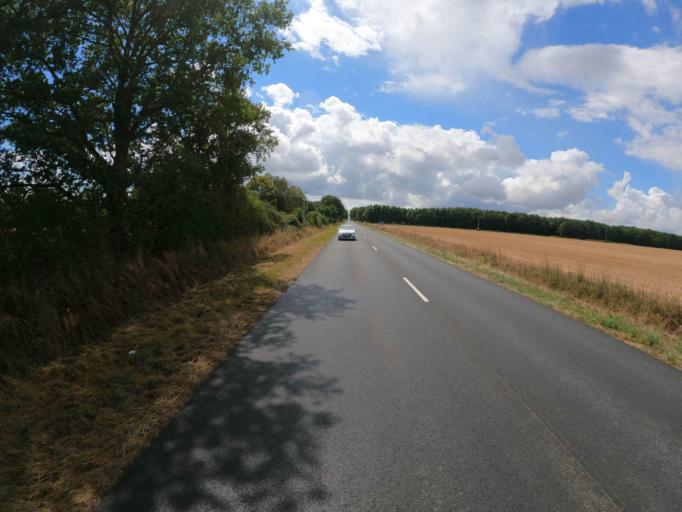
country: FR
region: Pays de la Loire
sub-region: Departement de Maine-et-Loire
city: Feneu
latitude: 47.5877
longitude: -0.5902
